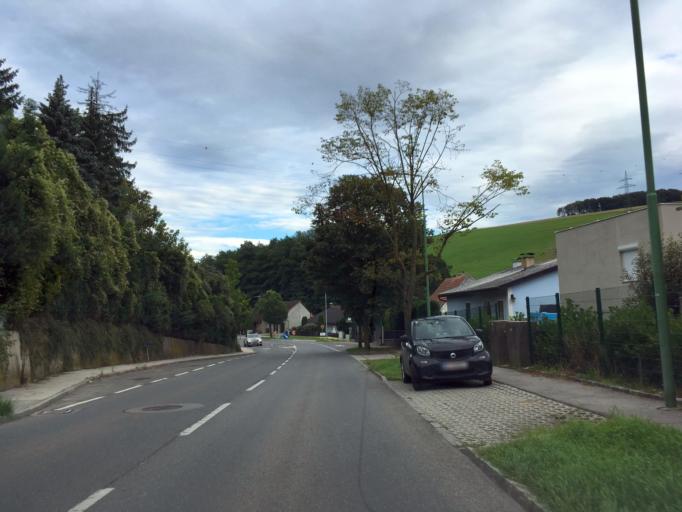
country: AT
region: Lower Austria
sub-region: Politischer Bezirk Tulln
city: Wordern
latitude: 48.3152
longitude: 16.2403
